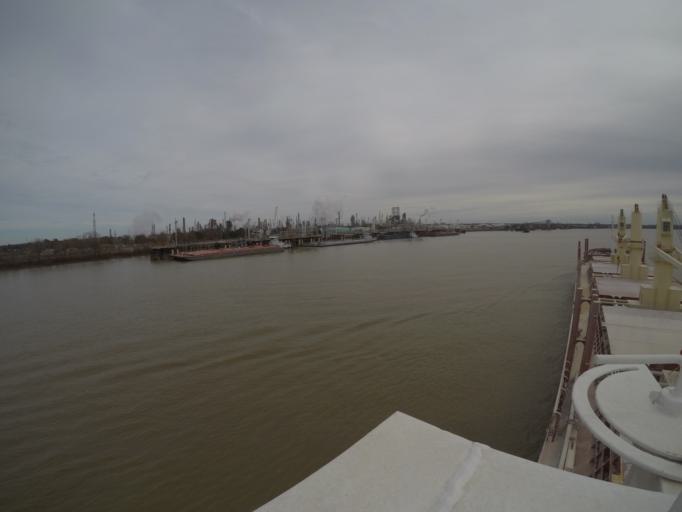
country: US
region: Louisiana
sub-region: Saint Charles Parish
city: Norco
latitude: 29.9932
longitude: -90.4140
